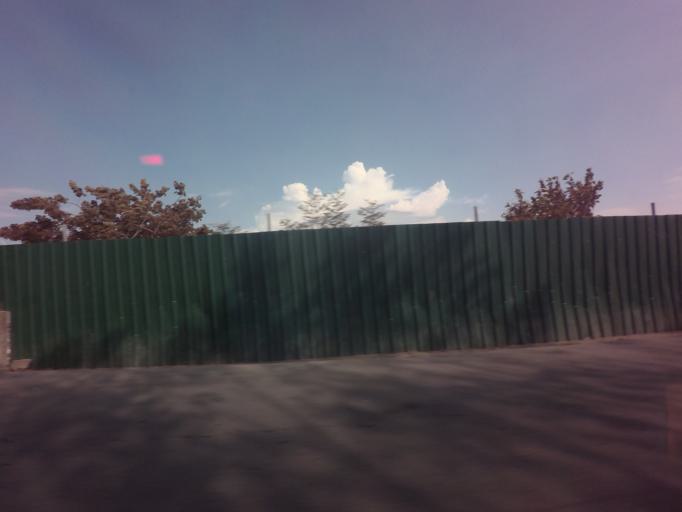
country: PH
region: Calabarzon
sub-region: Province of Rizal
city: Taguig
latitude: 14.5080
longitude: 121.0419
